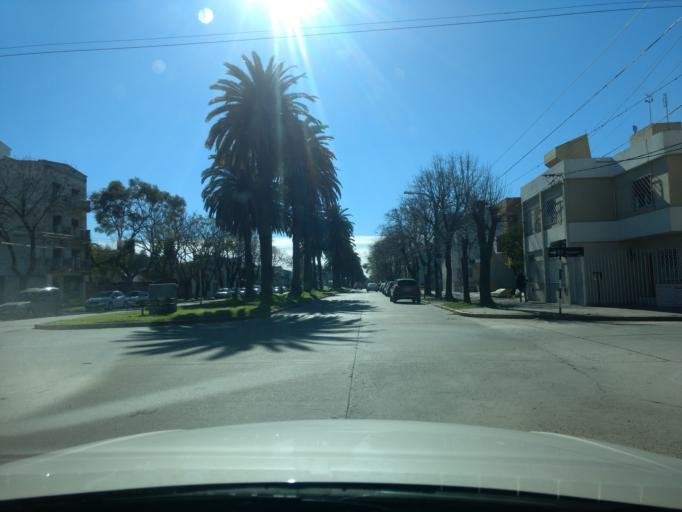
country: AR
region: Buenos Aires
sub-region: Partido de Lujan
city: Lujan
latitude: -34.5705
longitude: -59.1125
